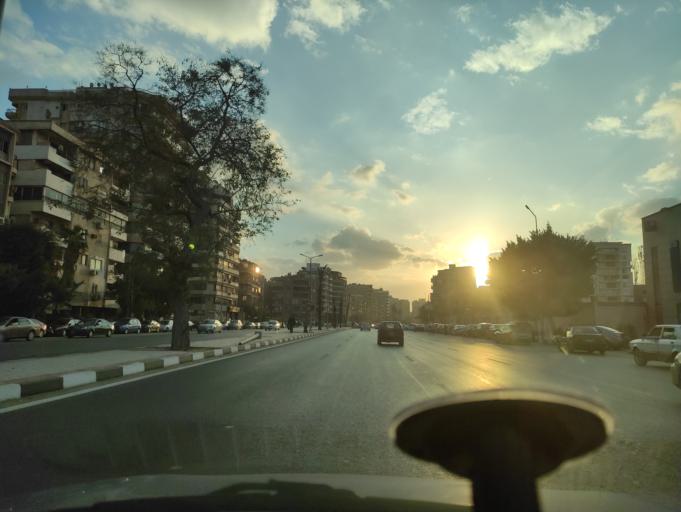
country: EG
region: Muhafazat al Qalyubiyah
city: Al Khankah
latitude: 30.1158
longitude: 31.3449
